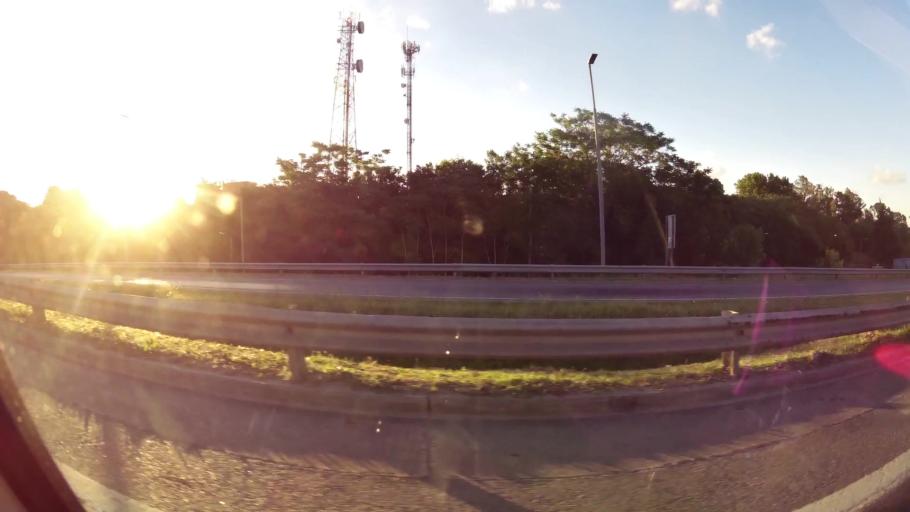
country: AR
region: Buenos Aires
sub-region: Partido de Quilmes
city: Quilmes
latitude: -34.7883
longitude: -58.1557
